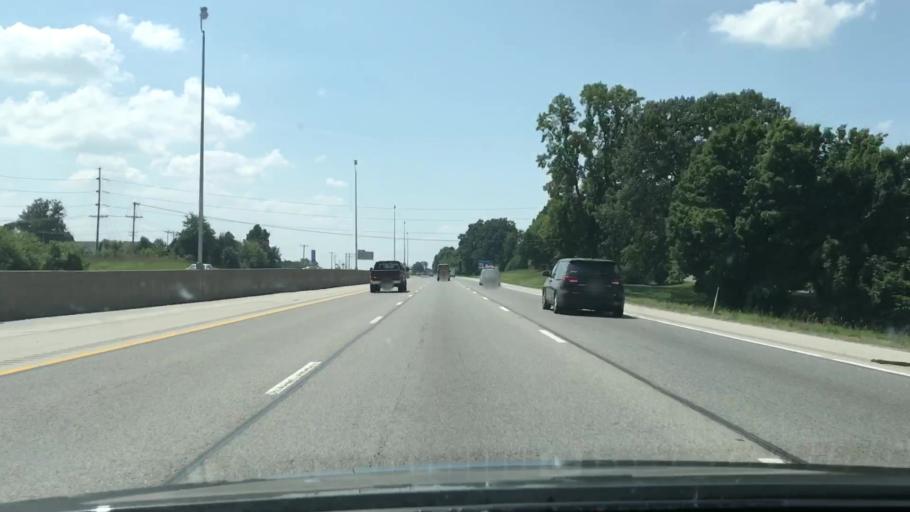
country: US
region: Kentucky
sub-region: Warren County
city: Bowling Green
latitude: 36.9504
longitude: -86.4077
